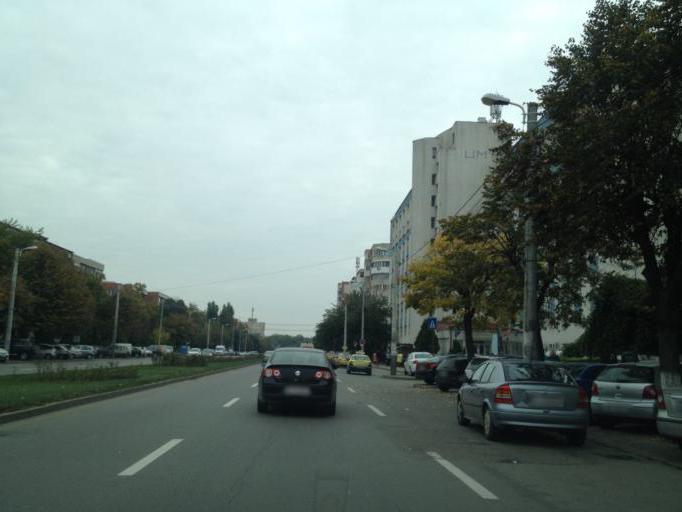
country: RO
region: Dolj
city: Craiova
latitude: 44.3055
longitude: 23.7947
